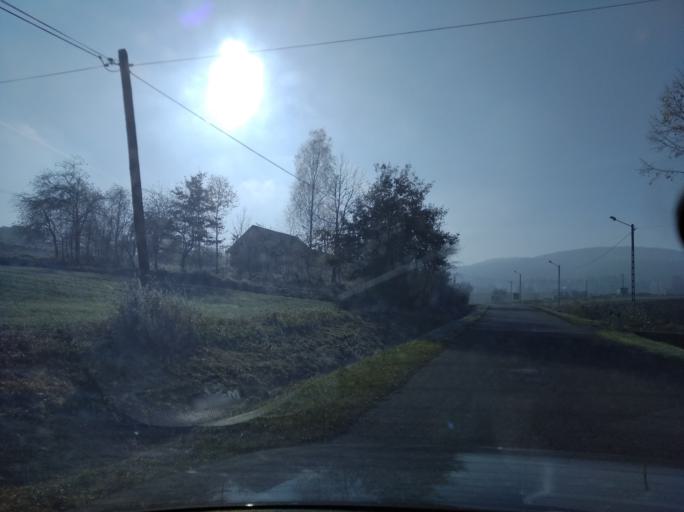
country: PL
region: Subcarpathian Voivodeship
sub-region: Powiat strzyzowski
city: Wysoka Strzyzowska
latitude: 49.8505
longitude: 21.7011
